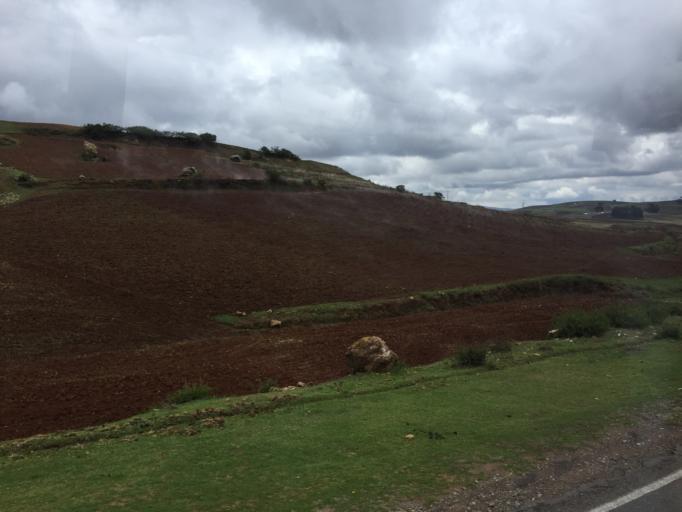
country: PE
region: Cusco
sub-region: Provincia de Urubamba
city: Huayllabamba
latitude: -13.3643
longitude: -72.0681
